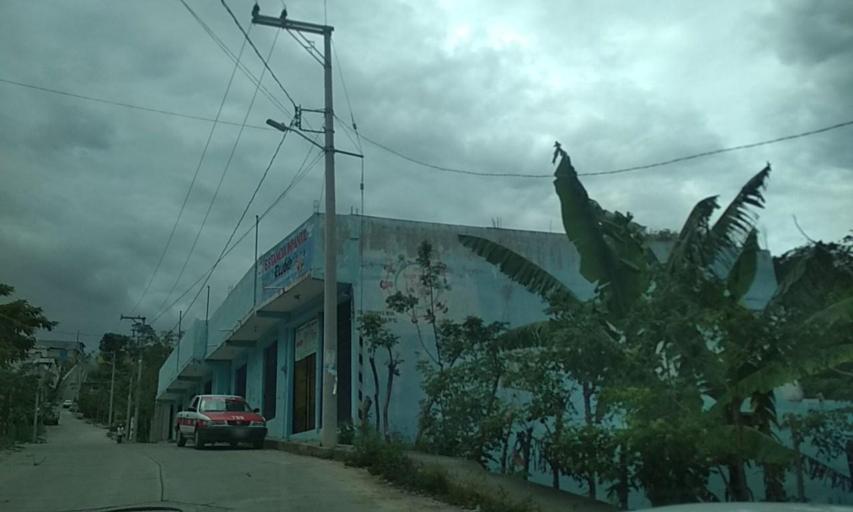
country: MX
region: Veracruz
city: Papantla de Olarte
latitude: 20.4575
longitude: -97.3144
